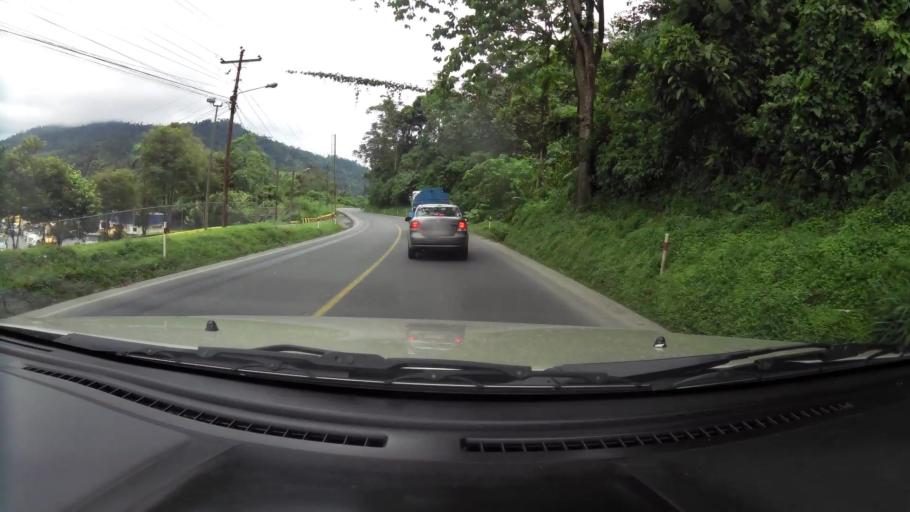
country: EC
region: Santo Domingo de los Tsachilas
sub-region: Canton Santo Domingo de los Colorados
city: Santo Domingo de los Colorados
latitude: -0.2723
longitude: -79.0978
